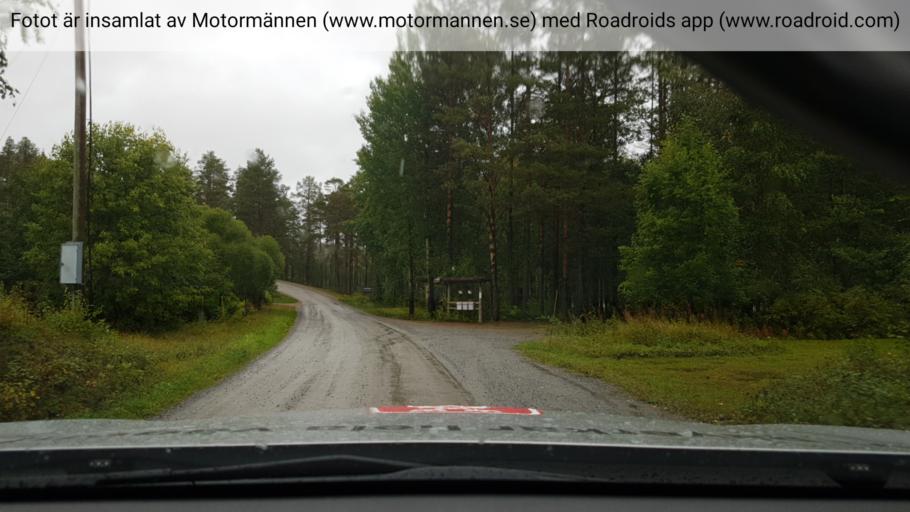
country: SE
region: Vaesterbotten
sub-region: Asele Kommun
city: Asele
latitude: 64.0226
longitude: 17.6603
